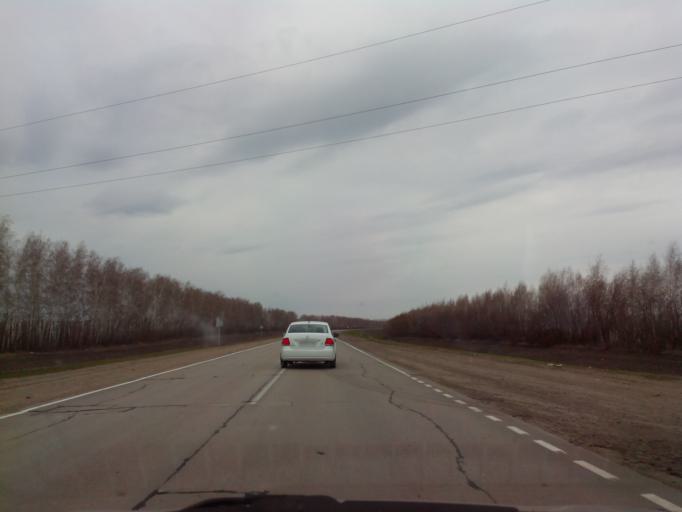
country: RU
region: Tambov
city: Znamenka
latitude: 52.4084
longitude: 41.3841
